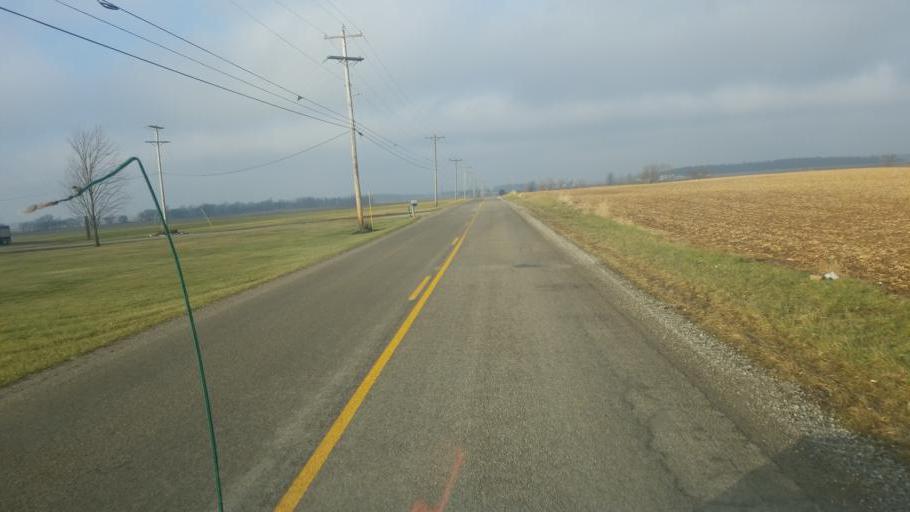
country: US
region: Ohio
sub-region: Hardin County
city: Kenton
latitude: 40.6620
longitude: -83.5762
